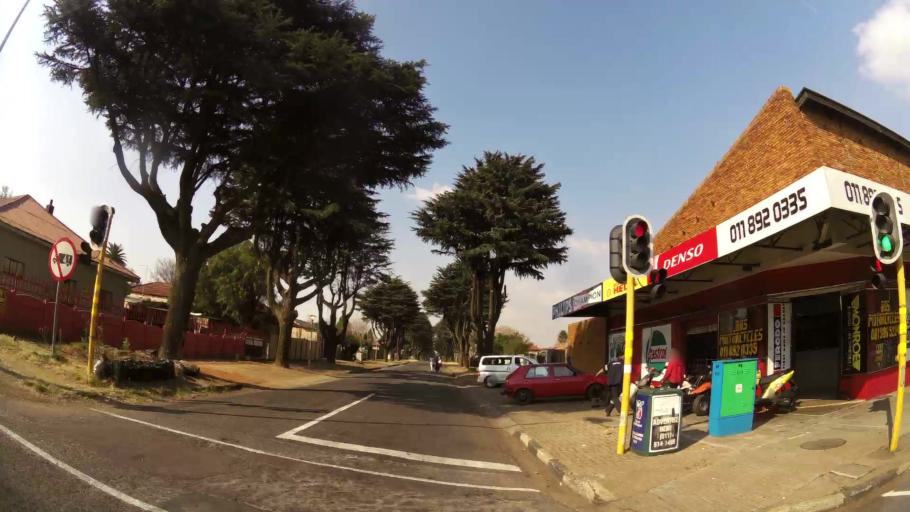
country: ZA
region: Gauteng
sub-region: Ekurhuleni Metropolitan Municipality
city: Boksburg
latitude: -26.2028
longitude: 28.2539
